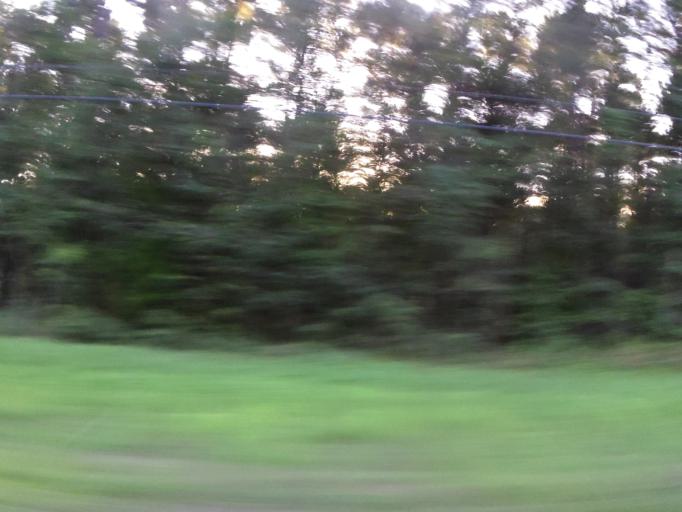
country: US
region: Georgia
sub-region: Camden County
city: Woodbine
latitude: 31.0601
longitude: -81.7289
